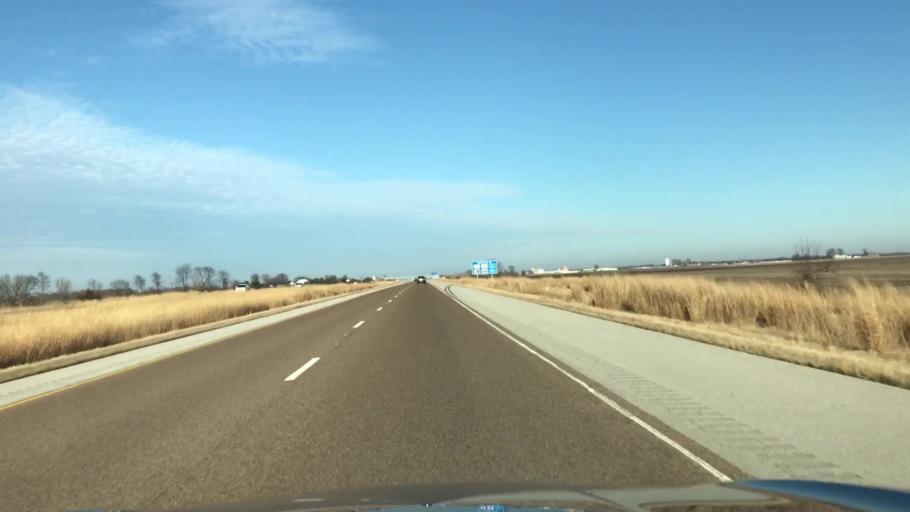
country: US
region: Illinois
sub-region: Montgomery County
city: Litchfield
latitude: 39.1438
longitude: -89.7029
